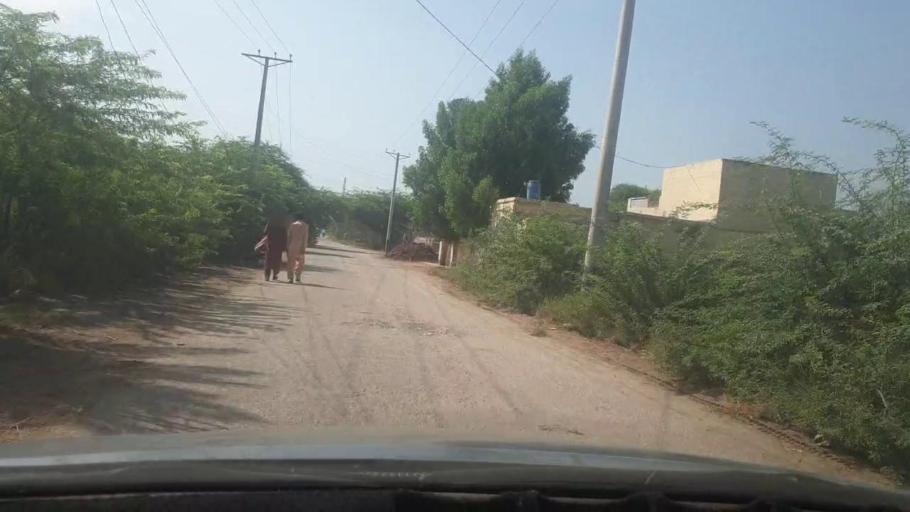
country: PK
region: Sindh
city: Gambat
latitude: 27.3332
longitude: 68.5475
